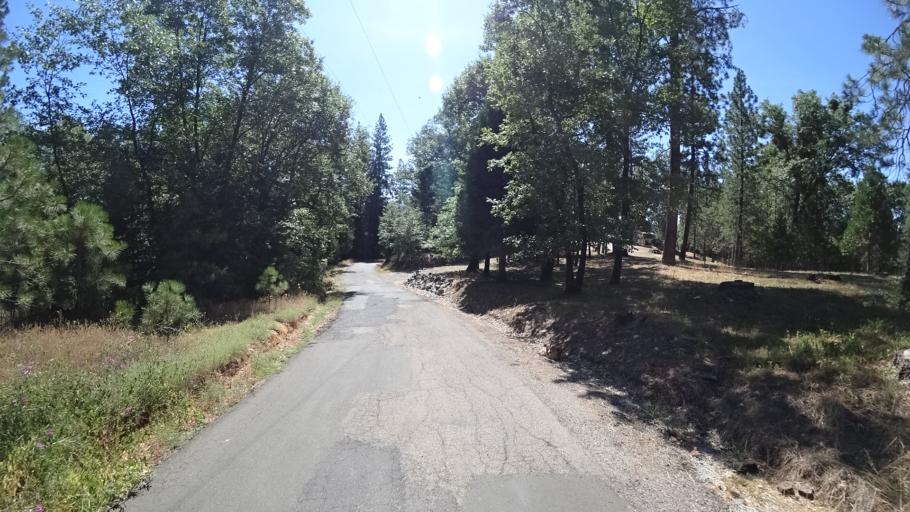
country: US
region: California
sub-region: Amador County
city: Pioneer
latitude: 38.3939
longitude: -120.5035
